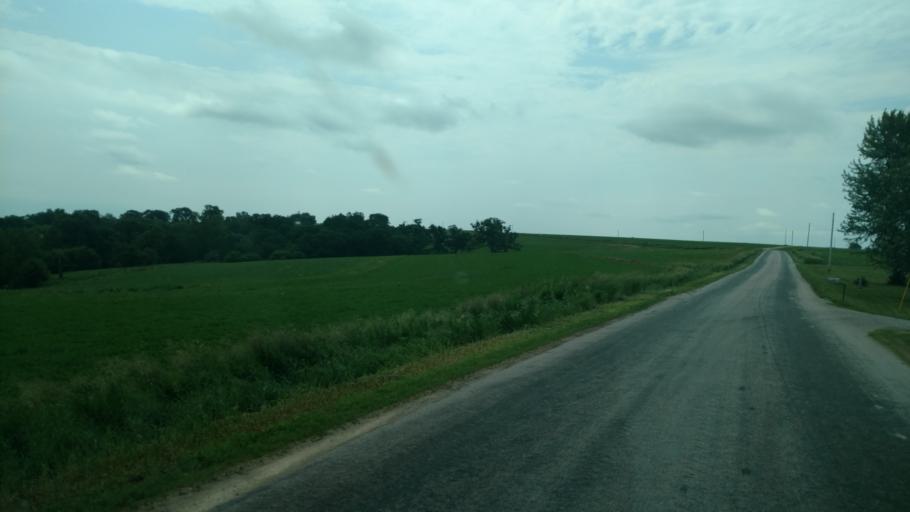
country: US
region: Wisconsin
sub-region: Monroe County
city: Cashton
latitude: 43.7765
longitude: -90.6664
